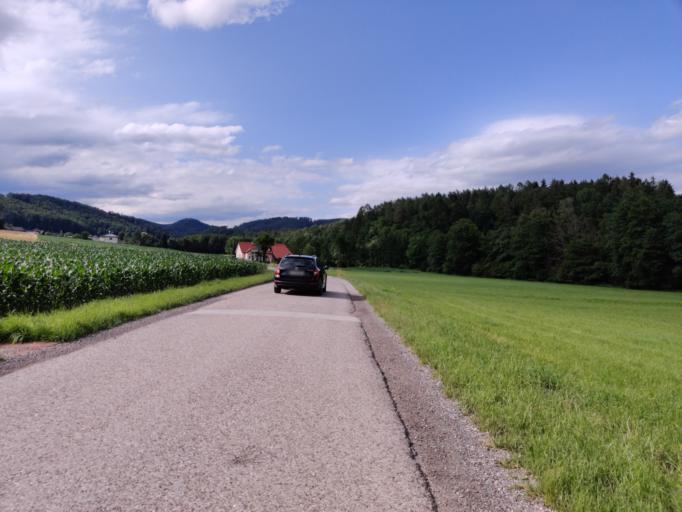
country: AT
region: Styria
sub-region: Politischer Bezirk Graz-Umgebung
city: Thal
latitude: 47.0674
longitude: 15.3386
